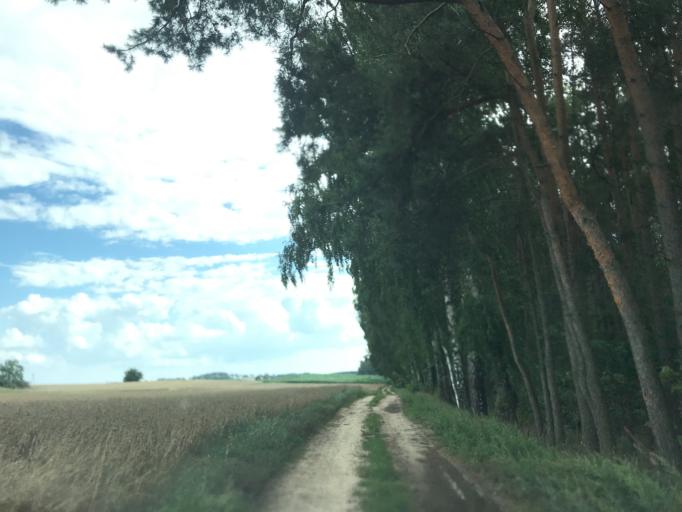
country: PL
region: Kujawsko-Pomorskie
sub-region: Powiat brodnicki
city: Brzozie
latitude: 53.3200
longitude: 19.6883
